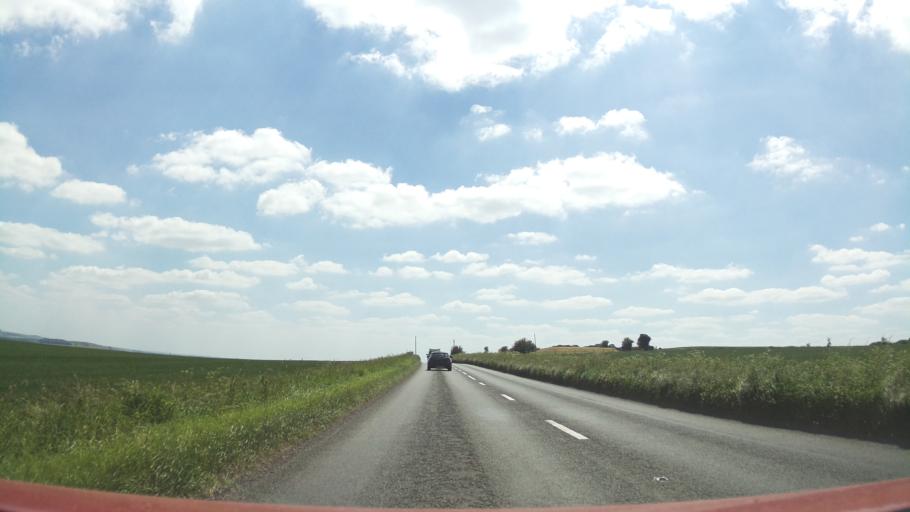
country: GB
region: England
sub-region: Wiltshire
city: Devizes
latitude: 51.3902
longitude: -1.9432
